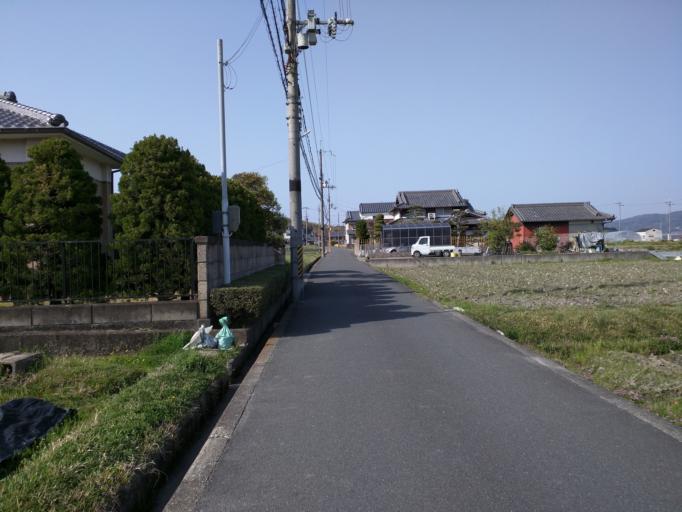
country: JP
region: Kyoto
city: Tanabe
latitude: 34.7633
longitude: 135.7841
